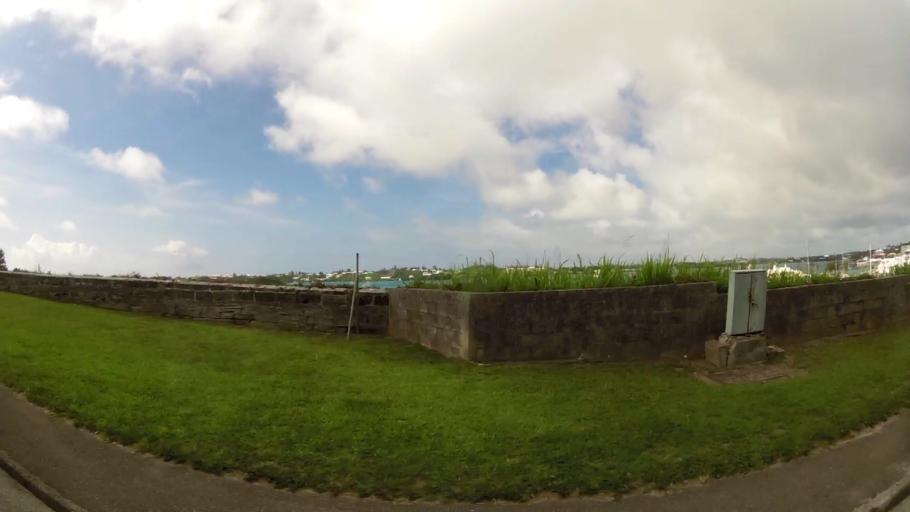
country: BM
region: Saint George
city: Saint George
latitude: 32.3821
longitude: -64.6731
